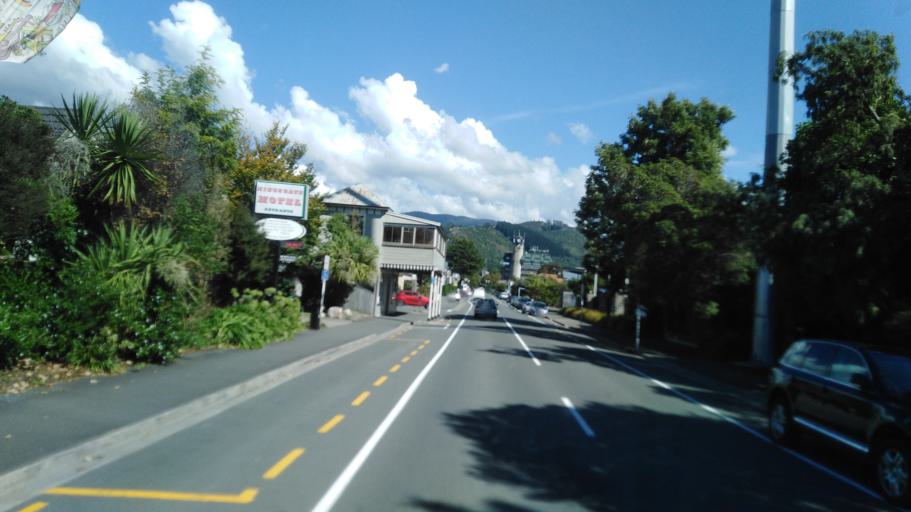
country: NZ
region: Nelson
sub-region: Nelson City
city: Nelson
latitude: -41.2669
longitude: 173.2841
